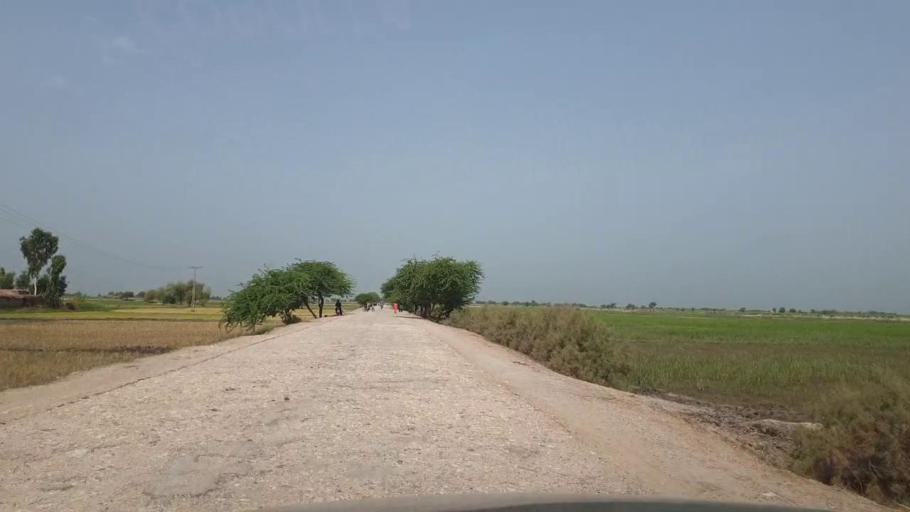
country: PK
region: Sindh
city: Garhi Yasin
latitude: 27.8578
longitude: 68.4137
